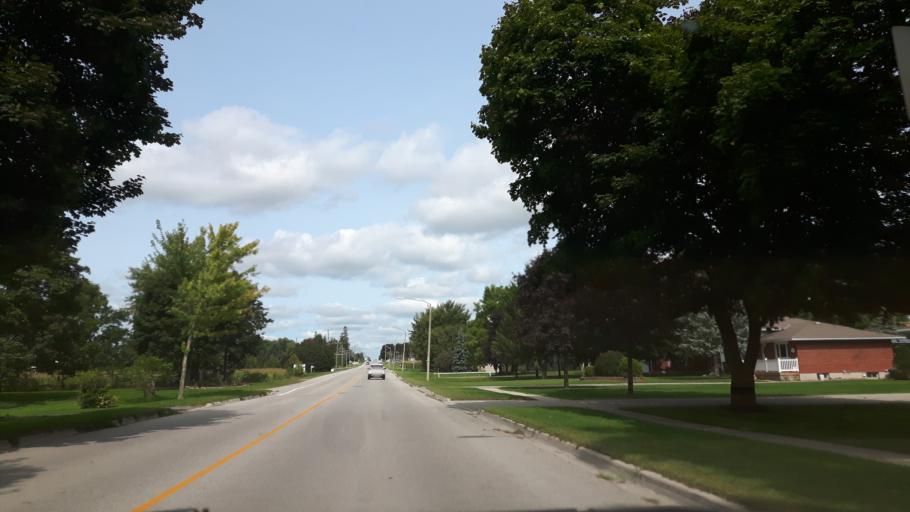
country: CA
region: Ontario
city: Huron East
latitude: 43.5591
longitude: -81.3885
